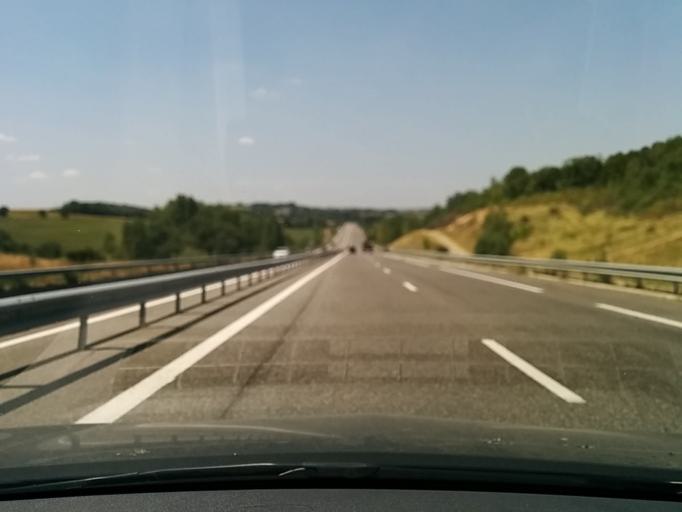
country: FR
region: Midi-Pyrenees
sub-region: Departement du Gers
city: Pujaudran
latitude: 43.5987
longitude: 1.1042
